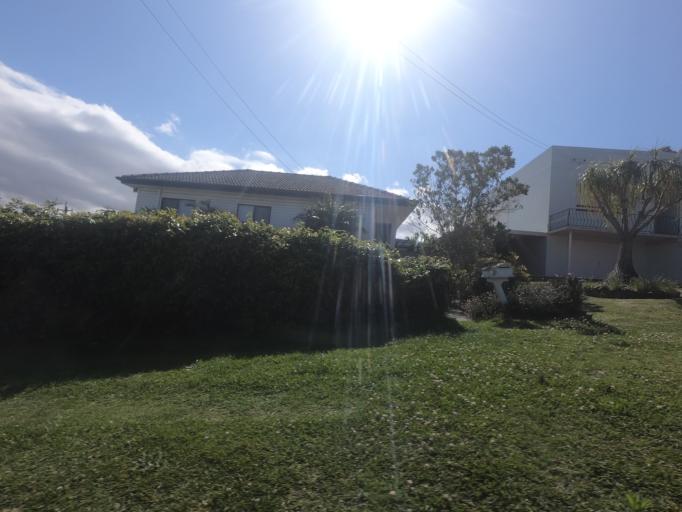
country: AU
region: New South Wales
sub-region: Wollongong
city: Cordeaux Heights
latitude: -34.4539
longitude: 150.8344
